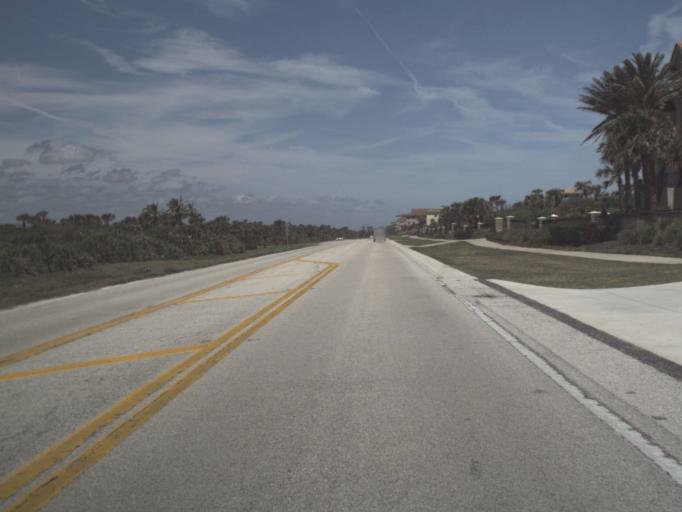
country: US
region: Florida
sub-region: Flagler County
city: Palm Coast
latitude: 29.5543
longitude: -81.1641
